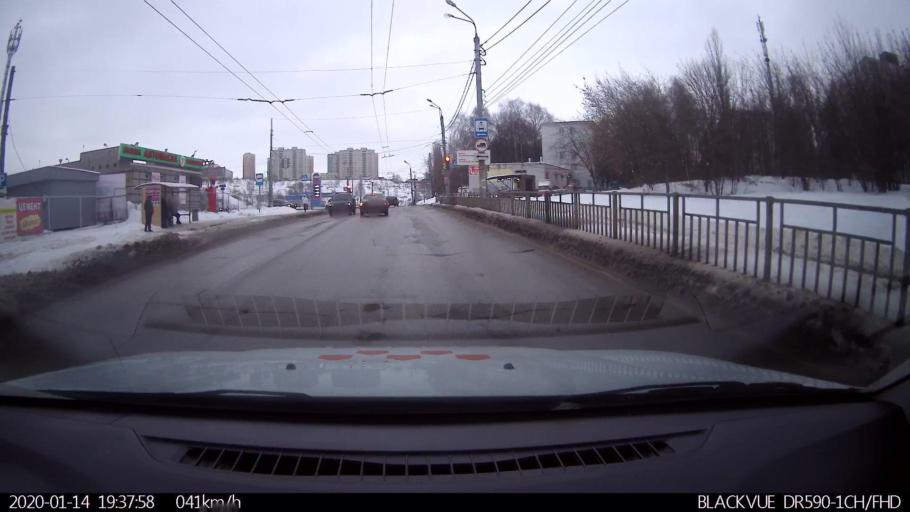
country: RU
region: Nizjnij Novgorod
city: Afonino
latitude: 56.2896
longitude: 44.0534
